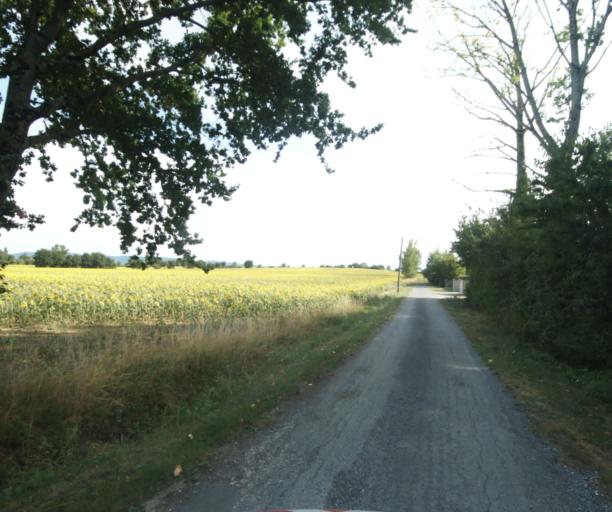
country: FR
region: Midi-Pyrenees
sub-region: Departement du Tarn
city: Puylaurens
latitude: 43.5168
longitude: 1.9986
